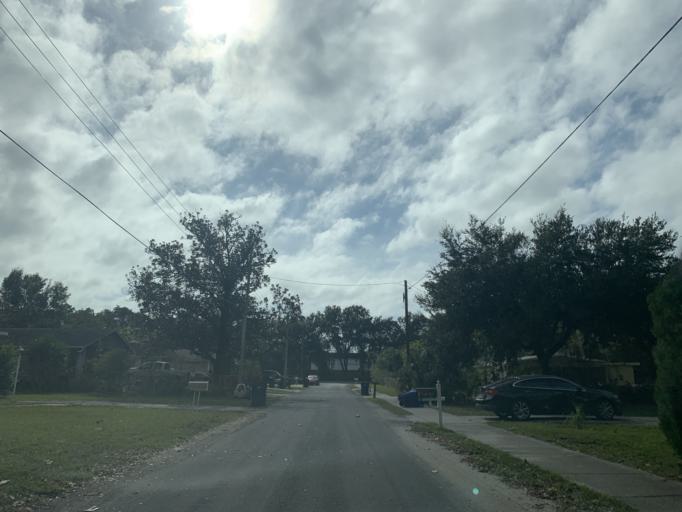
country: US
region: Florida
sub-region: Hillsborough County
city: East Lake-Orient Park
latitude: 27.9752
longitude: -82.4002
